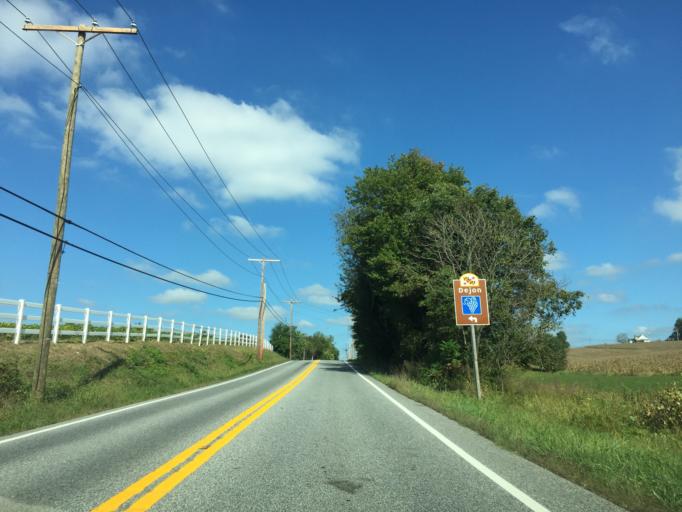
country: US
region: Maryland
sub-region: Baltimore County
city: Perry Hall
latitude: 39.4329
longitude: -76.4896
